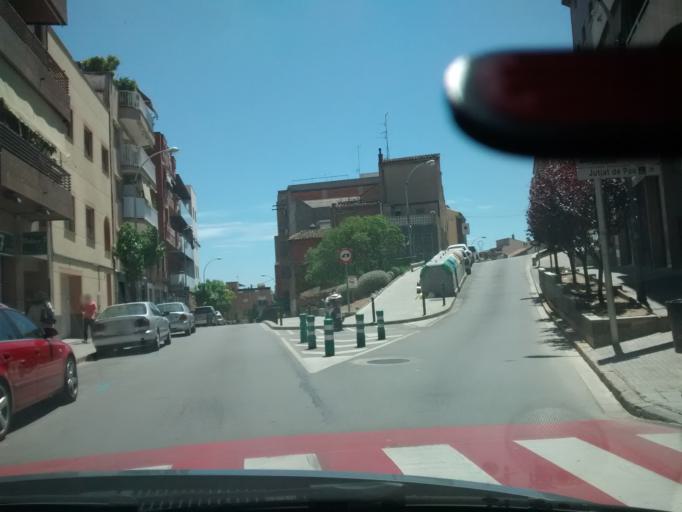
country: ES
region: Catalonia
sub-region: Provincia de Barcelona
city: Sant Vicenc dels Horts
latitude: 41.3944
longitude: 2.0092
